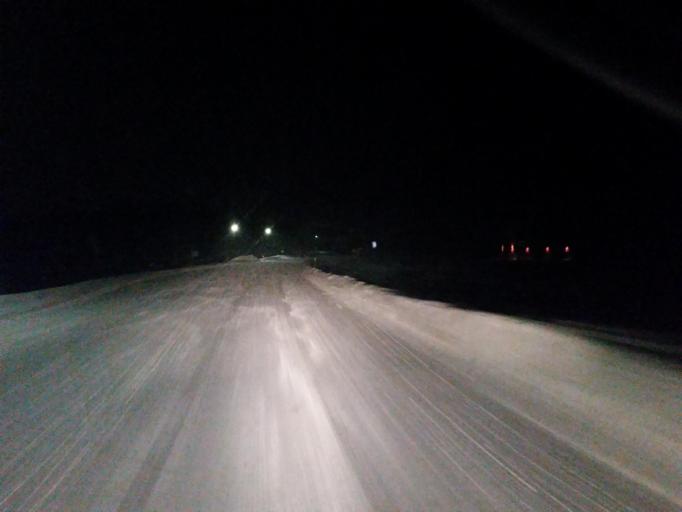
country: SE
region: Norrbotten
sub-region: Alvsbyns Kommun
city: AElvsbyn
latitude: 65.6936
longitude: 20.6658
